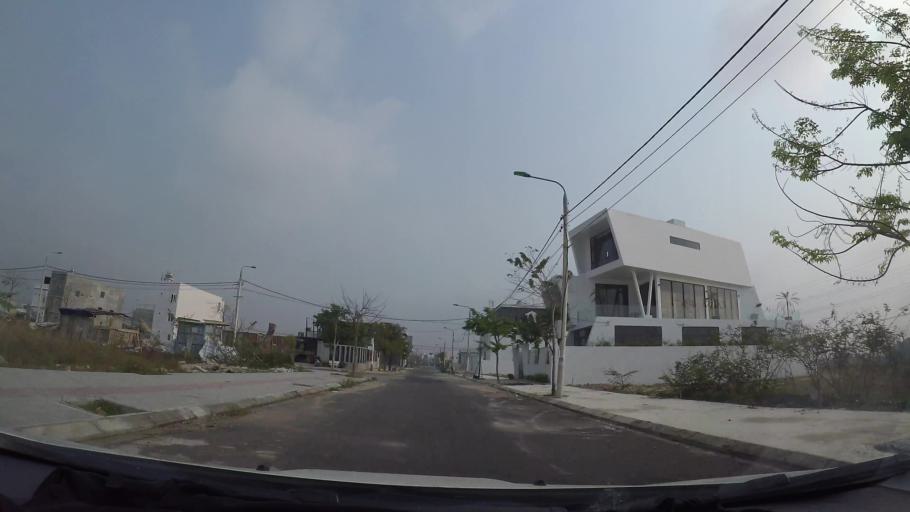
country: VN
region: Da Nang
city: Ngu Hanh Son
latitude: 16.0118
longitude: 108.2309
